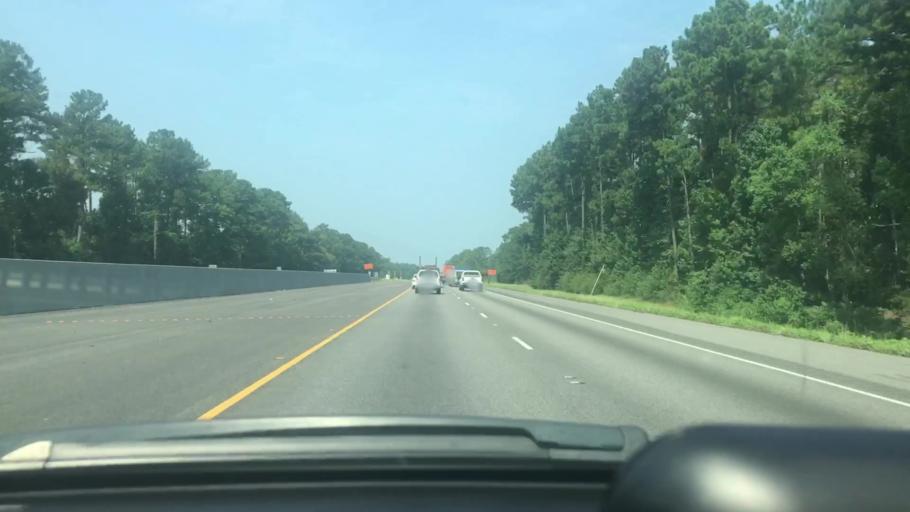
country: US
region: Louisiana
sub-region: Livingston Parish
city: Albany
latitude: 30.4747
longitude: -90.6567
